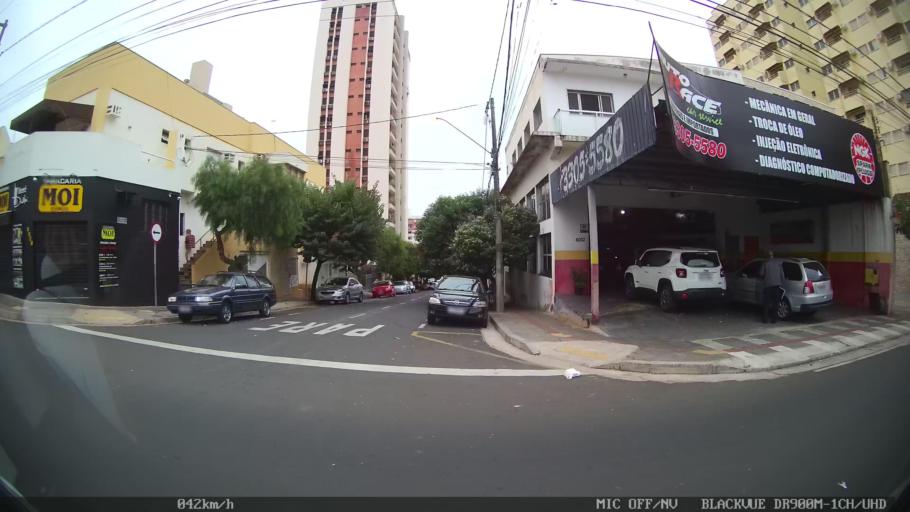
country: BR
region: Sao Paulo
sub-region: Sao Jose Do Rio Preto
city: Sao Jose do Rio Preto
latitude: -20.8168
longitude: -49.3880
